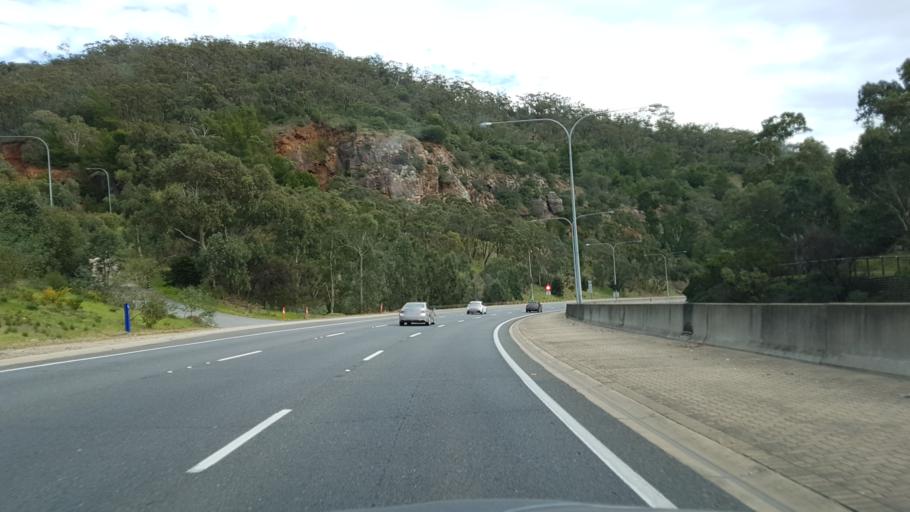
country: AU
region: South Australia
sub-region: Burnside
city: Mount Osmond
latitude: -34.9732
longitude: 138.6528
